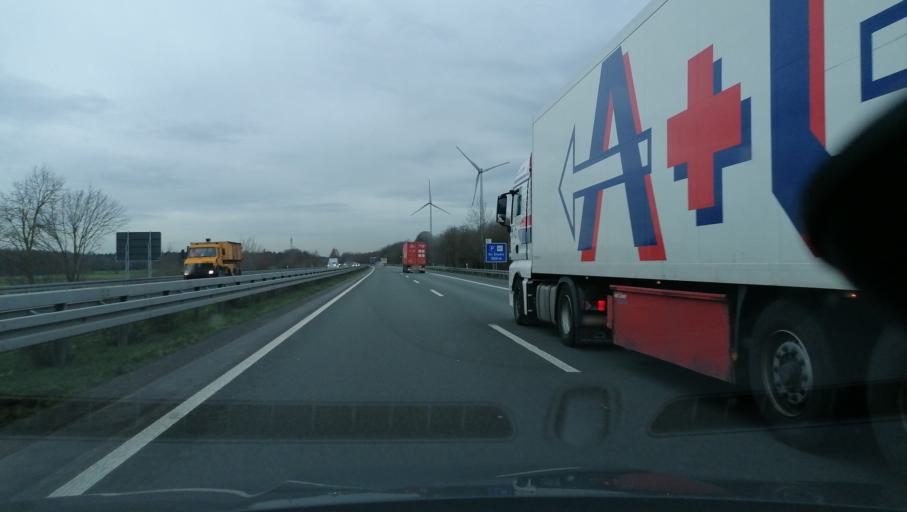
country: DE
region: North Rhine-Westphalia
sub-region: Regierungsbezirk Munster
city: Heiden
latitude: 51.7967
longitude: 6.9751
